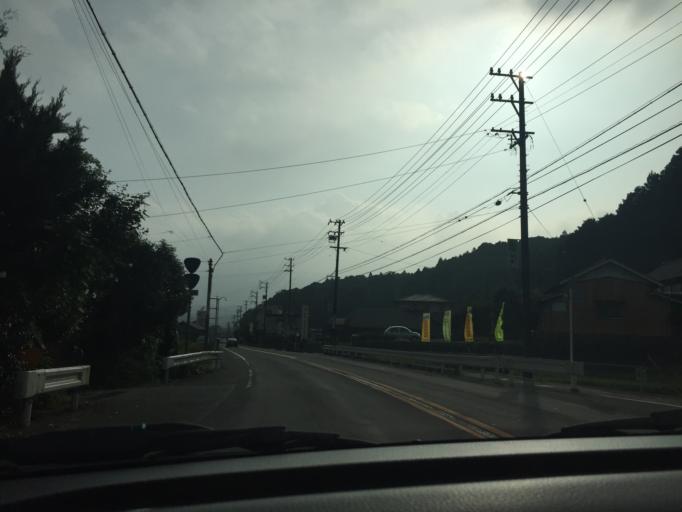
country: JP
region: Aichi
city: Shinshiro
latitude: 34.9286
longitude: 137.5656
